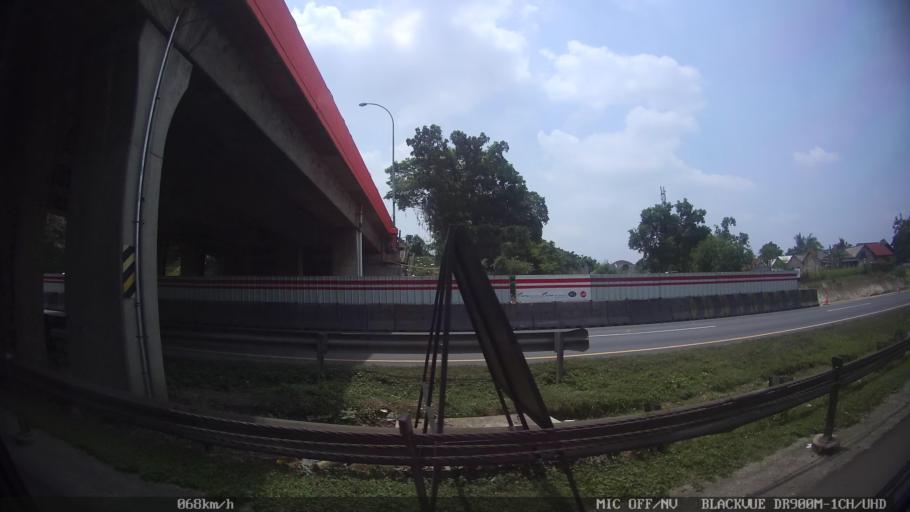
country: ID
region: West Java
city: Kresek
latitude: -6.1432
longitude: 106.2863
